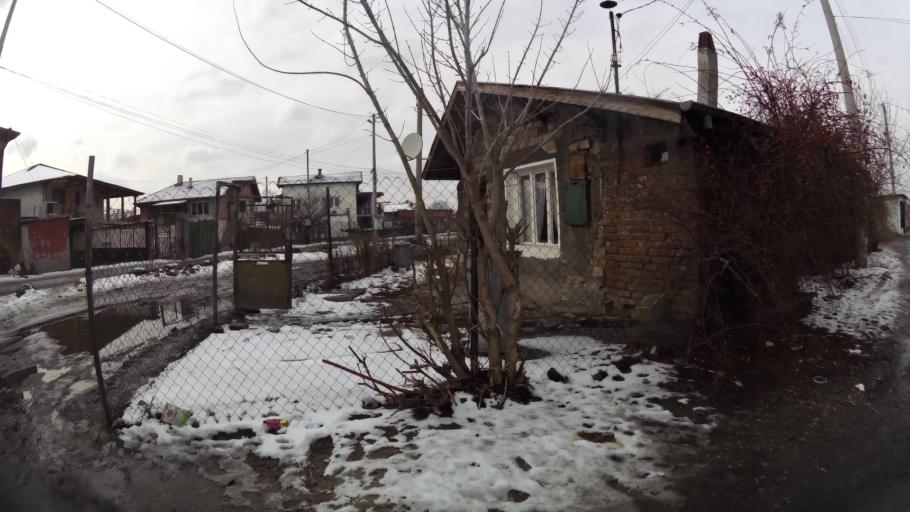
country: BG
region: Sofia-Capital
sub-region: Stolichna Obshtina
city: Sofia
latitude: 42.6934
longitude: 23.3827
